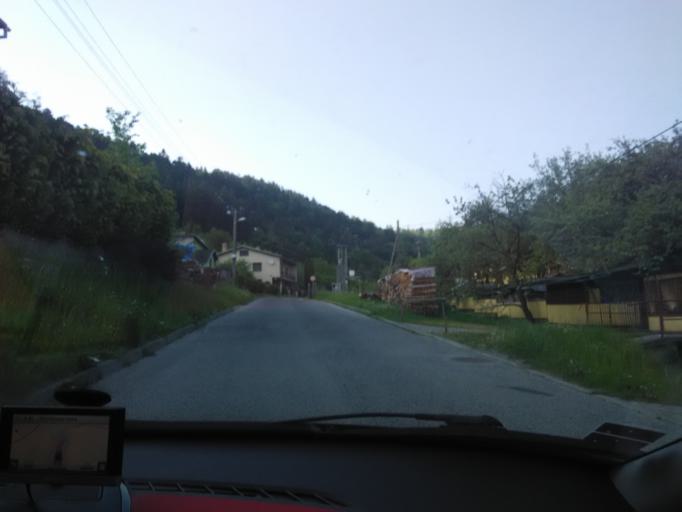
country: SK
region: Presovsky
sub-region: Okres Presov
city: Levoca
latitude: 49.0386
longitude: 20.6013
